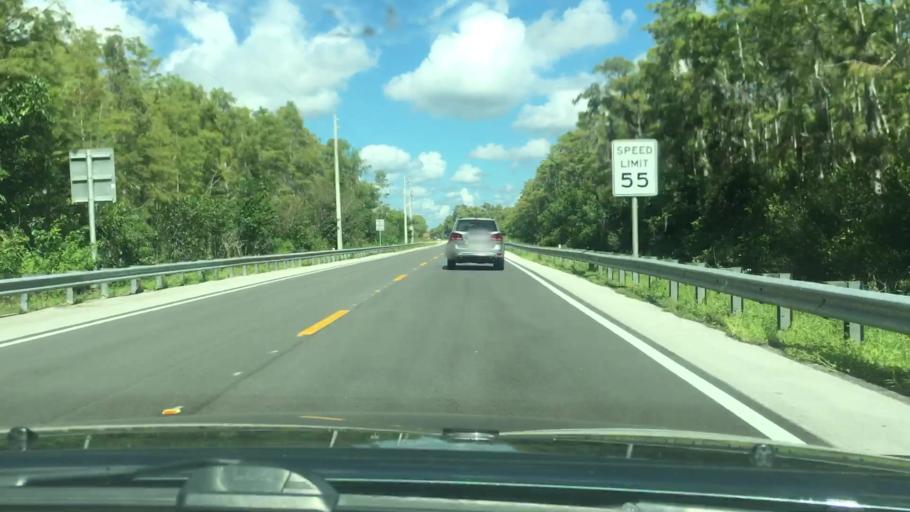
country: US
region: Florida
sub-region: Miami-Dade County
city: Kendall West
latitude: 25.8037
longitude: -80.8712
